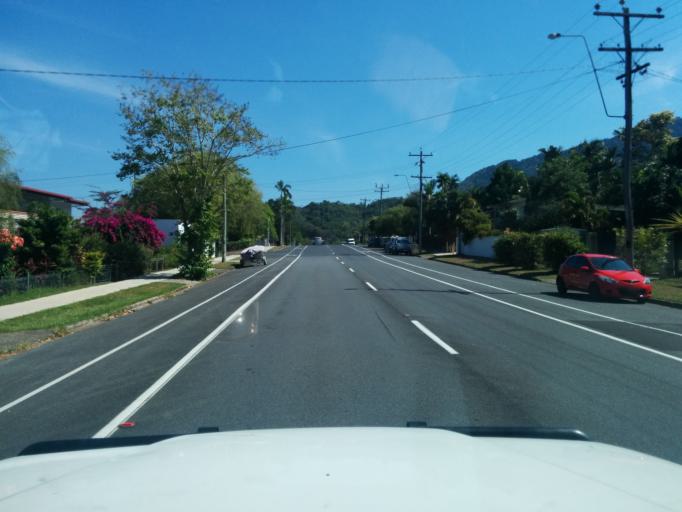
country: AU
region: Queensland
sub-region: Cairns
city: Redlynch
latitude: -16.9068
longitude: 145.7285
